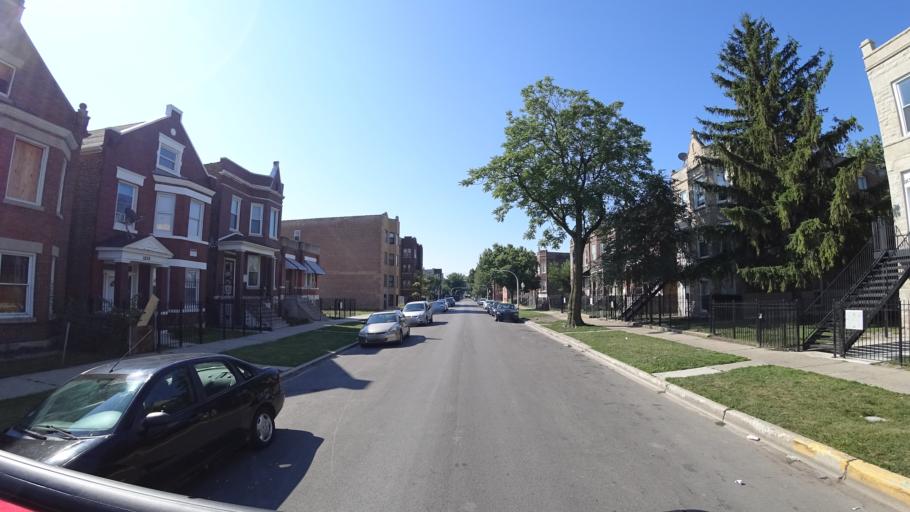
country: US
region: Illinois
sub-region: Cook County
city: Cicero
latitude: 41.8560
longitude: -87.7236
